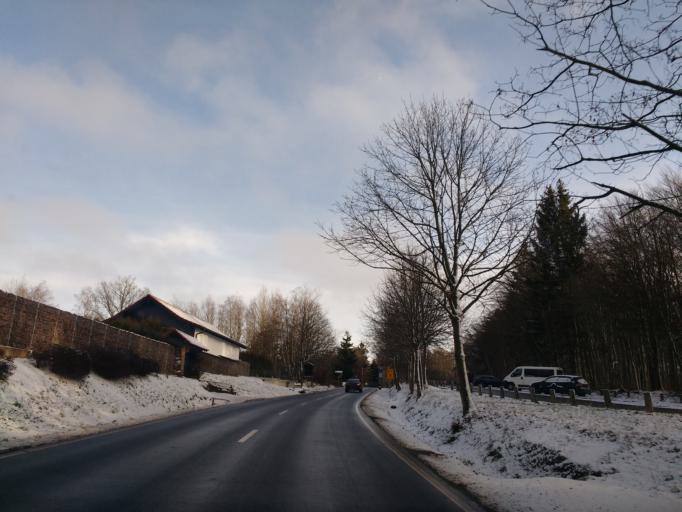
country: DE
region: Saxony-Anhalt
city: Friedrichsbrunn
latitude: 51.6942
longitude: 11.0480
